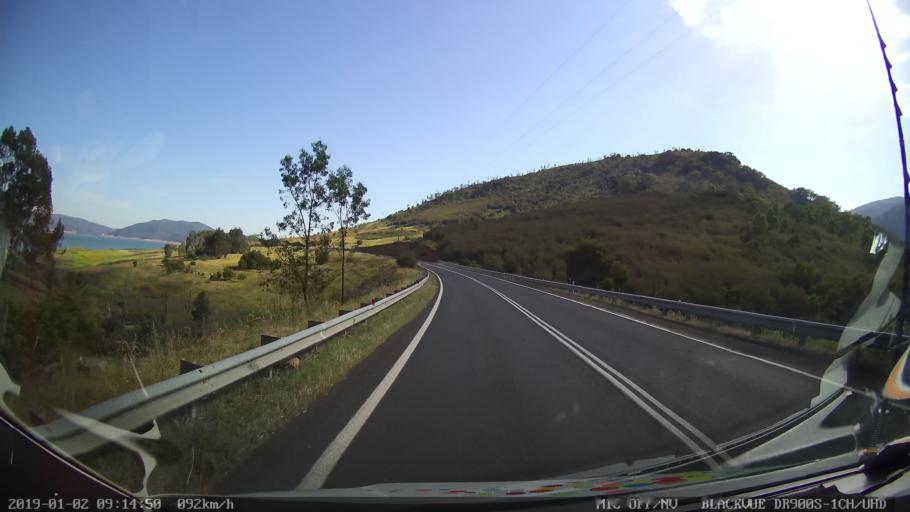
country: AU
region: New South Wales
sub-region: Tumut Shire
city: Tumut
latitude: -35.4725
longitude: 148.2778
